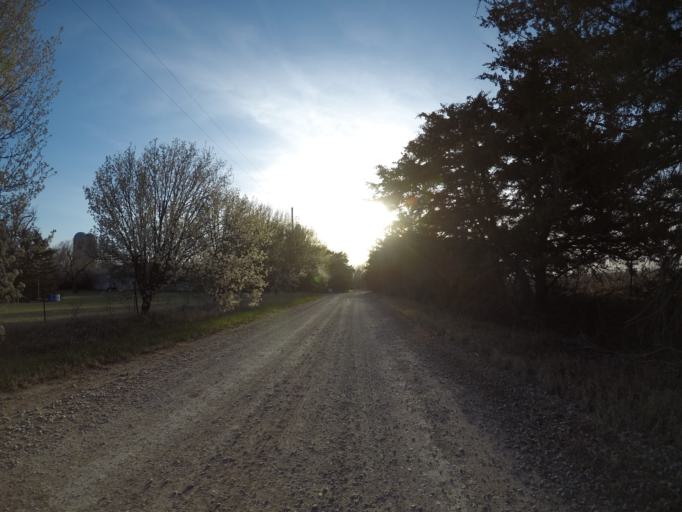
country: US
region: Kansas
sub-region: Riley County
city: Manhattan
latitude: 39.2472
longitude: -96.6926
